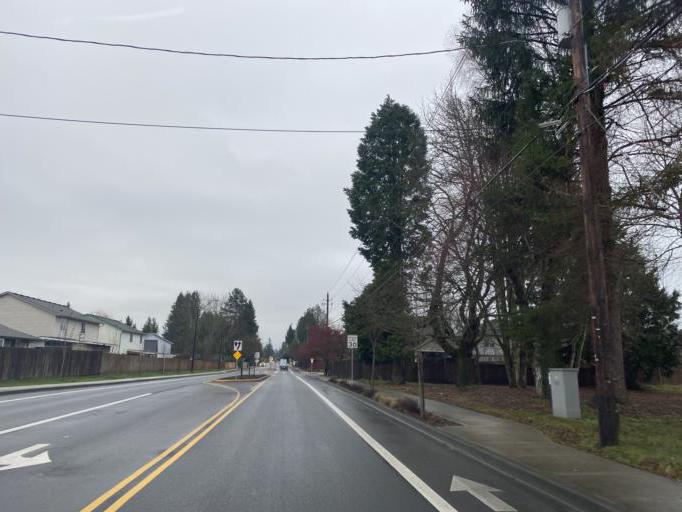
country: US
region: Washington
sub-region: Clark County
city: Battle Ground
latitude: 45.7749
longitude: -122.5374
